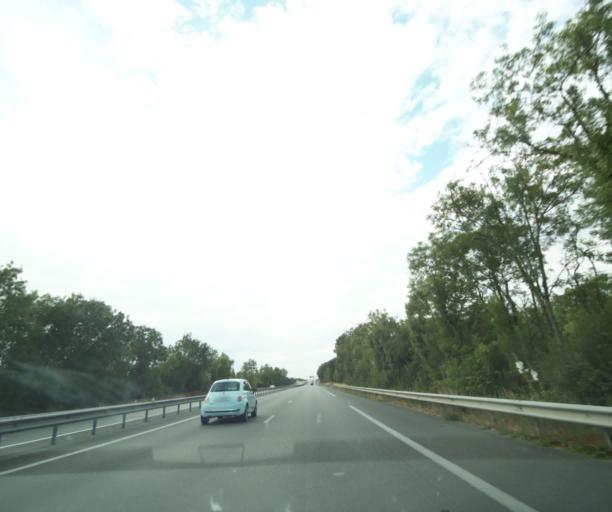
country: FR
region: Poitou-Charentes
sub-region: Departement de la Charente-Maritime
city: Angoulins
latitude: 46.0953
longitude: -1.0883
